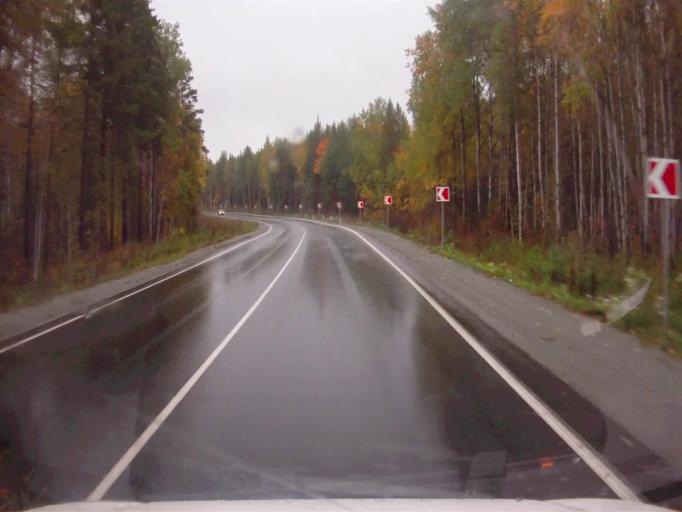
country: RU
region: Chelyabinsk
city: Tayginka
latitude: 55.6327
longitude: 60.5999
